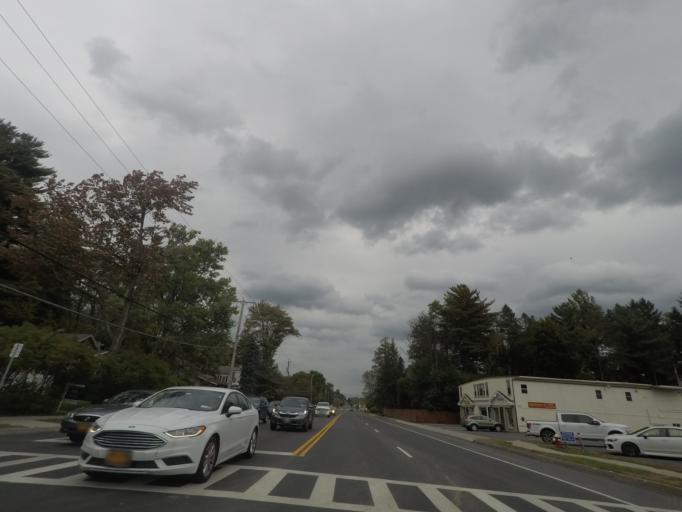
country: US
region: New York
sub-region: Albany County
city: McKownville
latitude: 42.6799
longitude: -73.8340
